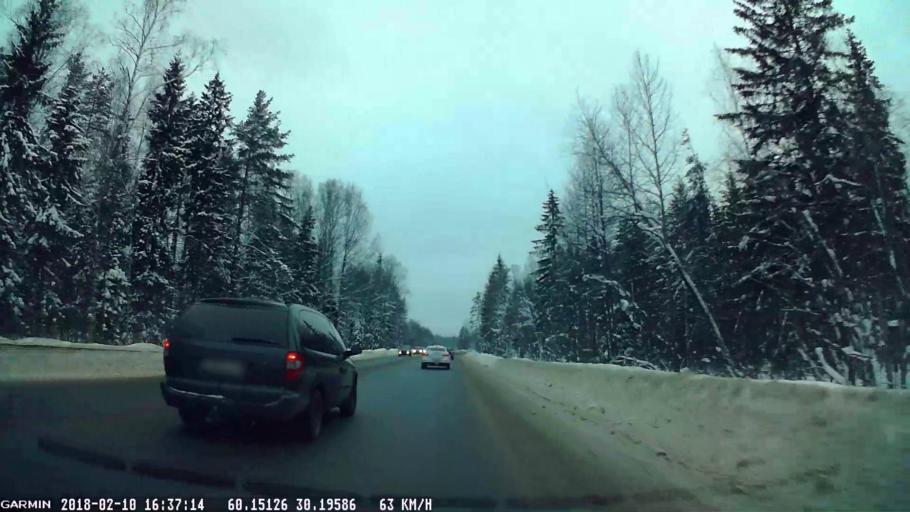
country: RU
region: Leningrad
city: Sertolovo
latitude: 60.1494
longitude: 30.1982
